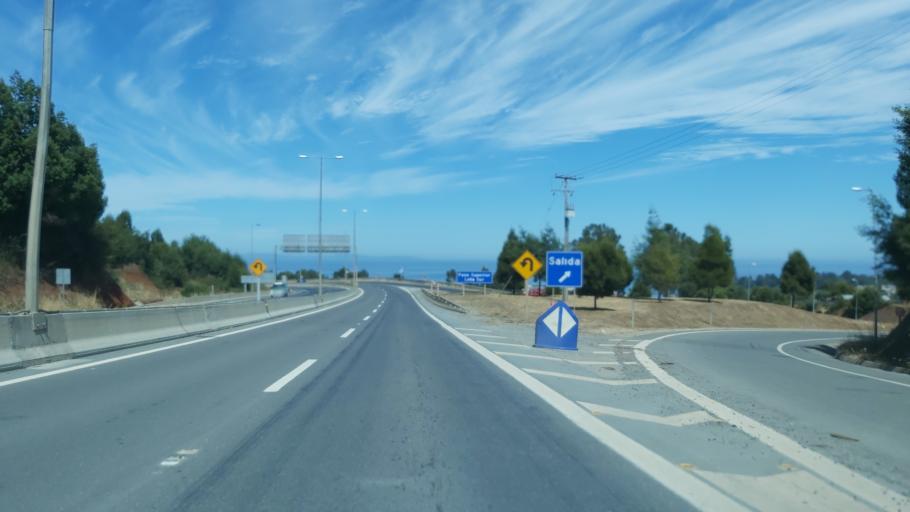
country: CL
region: Biobio
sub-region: Provincia de Concepcion
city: Lota
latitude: -37.0992
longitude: -73.1469
